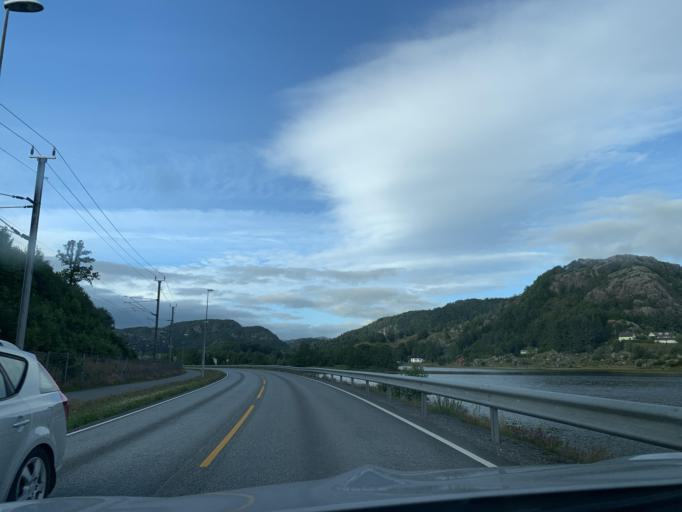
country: NO
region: Rogaland
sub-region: Eigersund
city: Egersund
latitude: 58.4636
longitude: 6.0214
